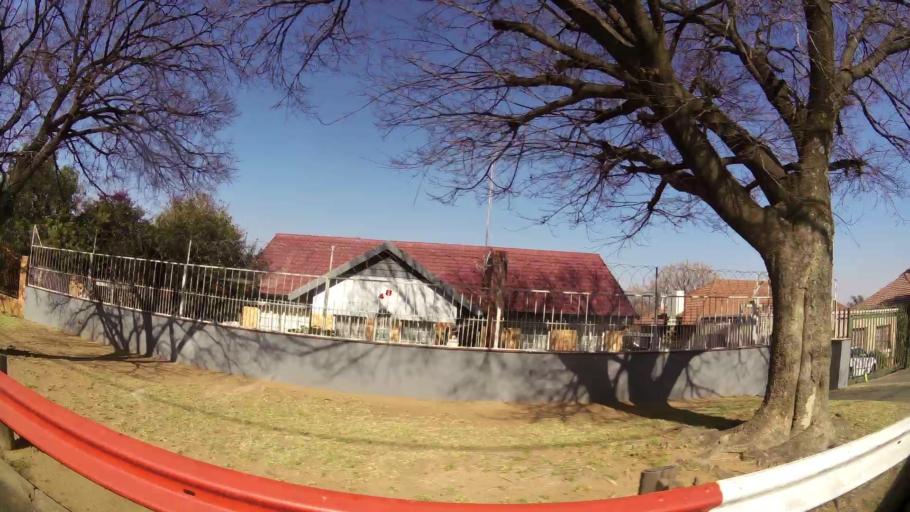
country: ZA
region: Gauteng
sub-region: City of Johannesburg Metropolitan Municipality
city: Johannesburg
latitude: -26.2622
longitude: 28.0653
